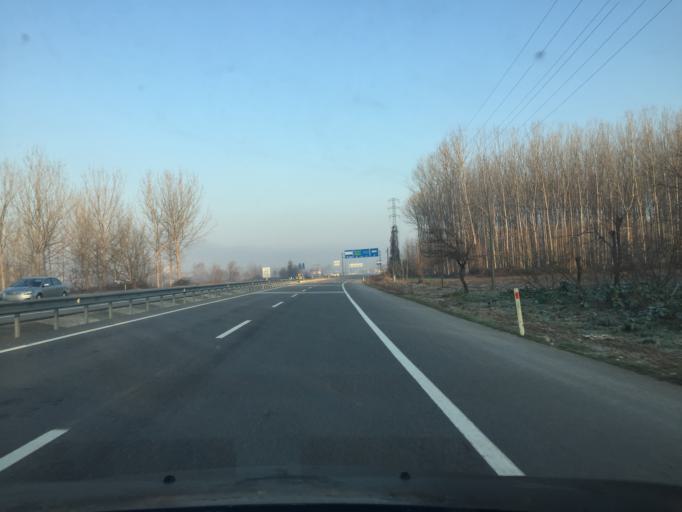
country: TR
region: Sakarya
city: Akyazi
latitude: 40.6564
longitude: 30.5985
